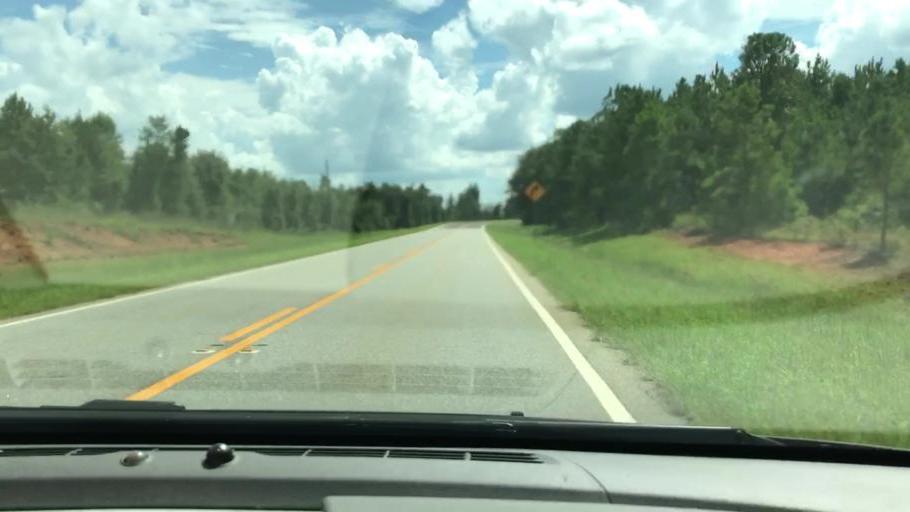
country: US
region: Georgia
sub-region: Quitman County
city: Georgetown
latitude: 31.9138
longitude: -85.0591
